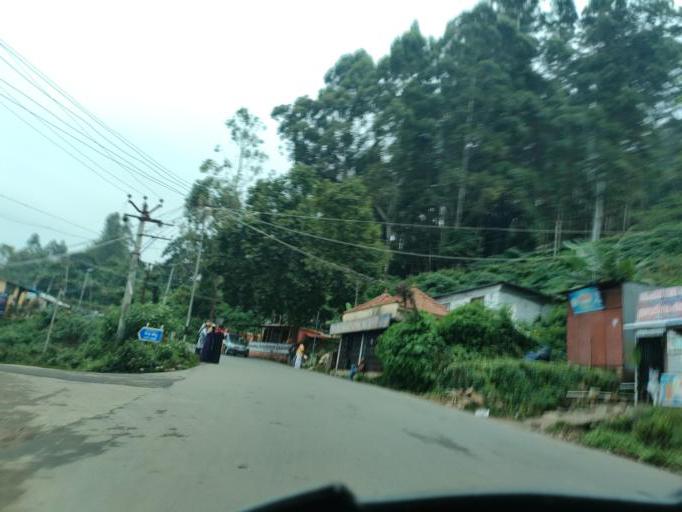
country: IN
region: Tamil Nadu
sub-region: Dindigul
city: Kodaikanal
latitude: 10.2324
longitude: 77.5029
